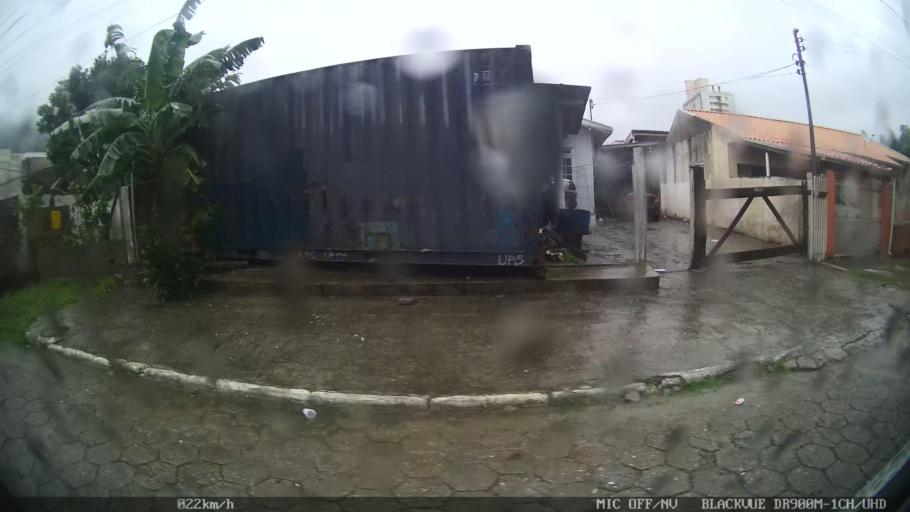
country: BR
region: Santa Catarina
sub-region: Itajai
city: Itajai
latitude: -26.9219
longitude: -48.6498
